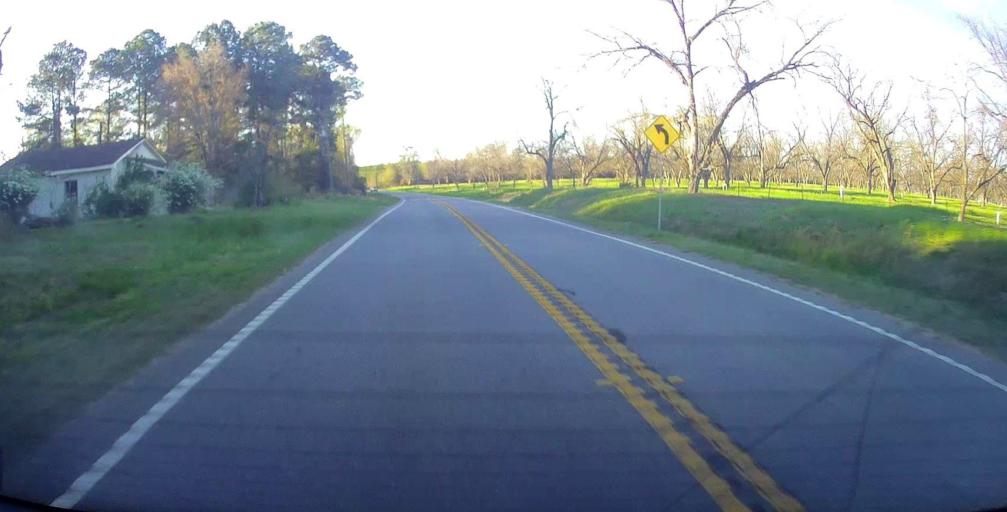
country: US
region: Georgia
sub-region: Wilcox County
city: Abbeville
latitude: 32.0328
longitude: -83.2520
